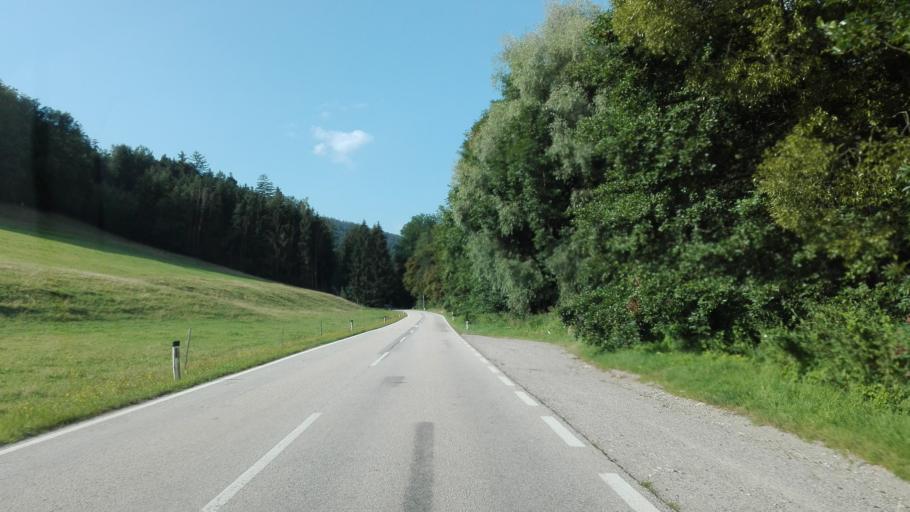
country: AT
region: Lower Austria
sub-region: Politischer Bezirk Sankt Polten
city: Stossing
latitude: 48.0879
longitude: 15.7832
